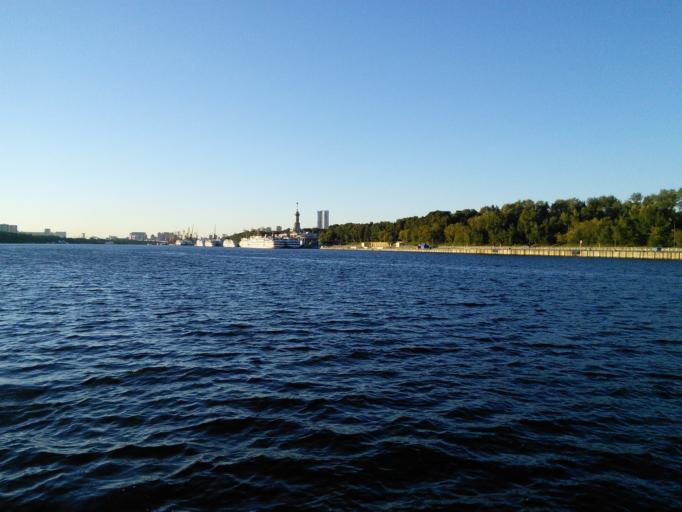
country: RU
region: Moskovskaya
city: Levoberezhnyy
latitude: 55.8441
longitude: 37.4677
